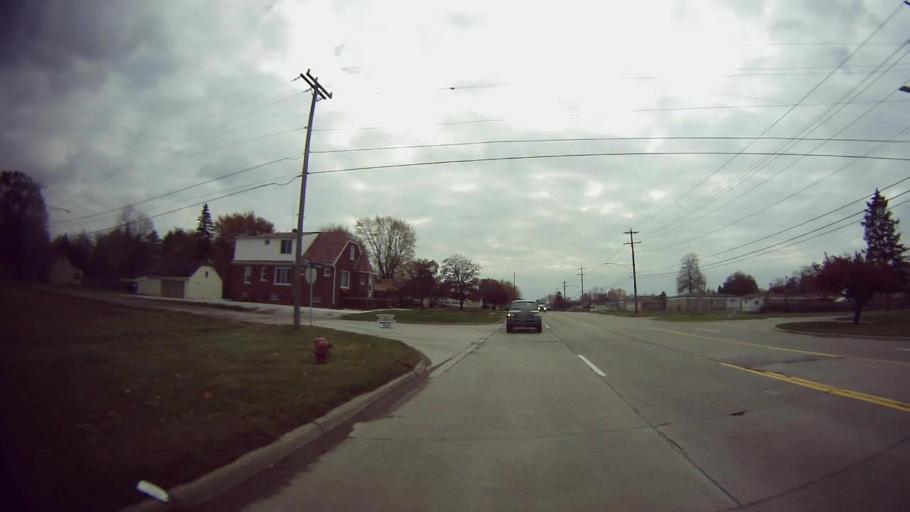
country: US
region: Michigan
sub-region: Oakland County
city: Madison Heights
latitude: 42.5331
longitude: -83.0684
